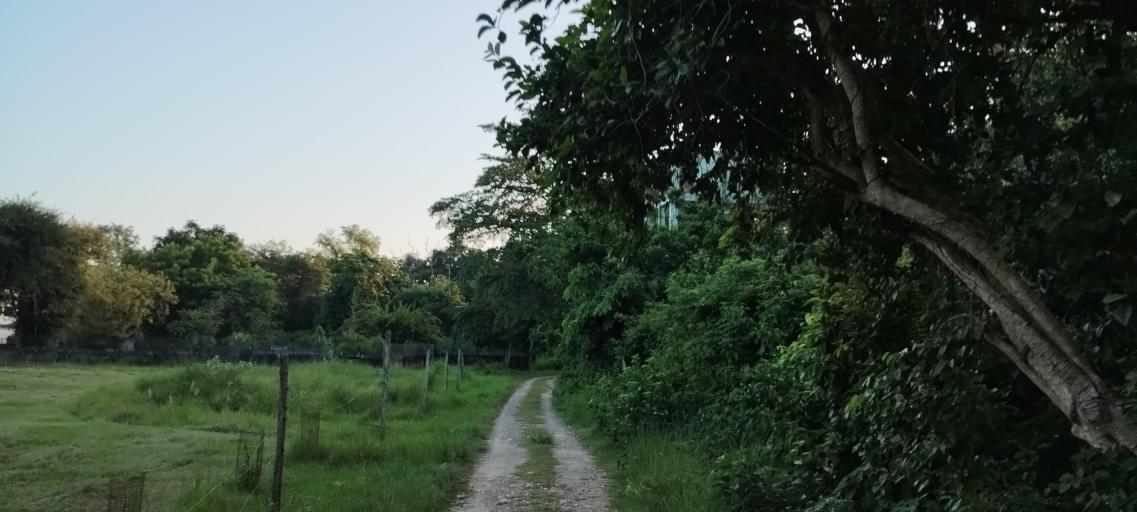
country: NP
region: Far Western
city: Tikapur
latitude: 28.4545
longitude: 81.2419
